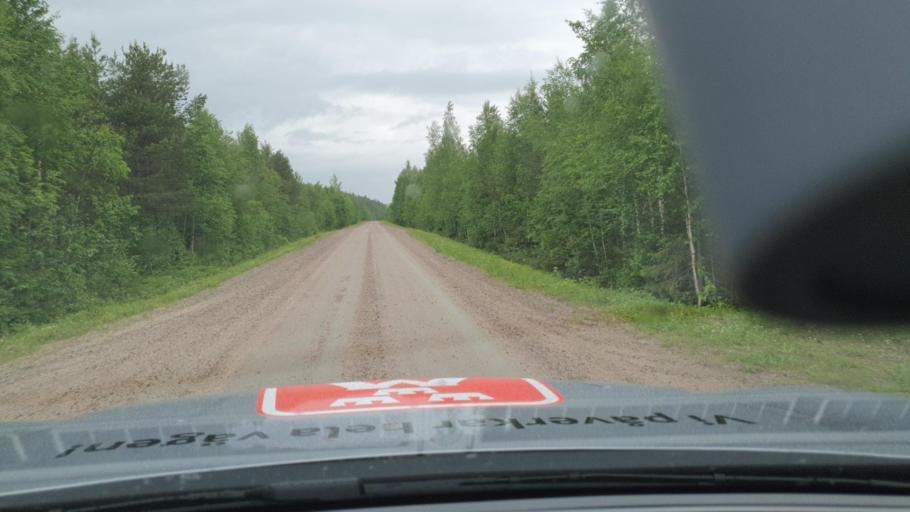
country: SE
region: Norrbotten
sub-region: Overkalix Kommun
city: OEverkalix
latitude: 66.5842
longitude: 22.7455
